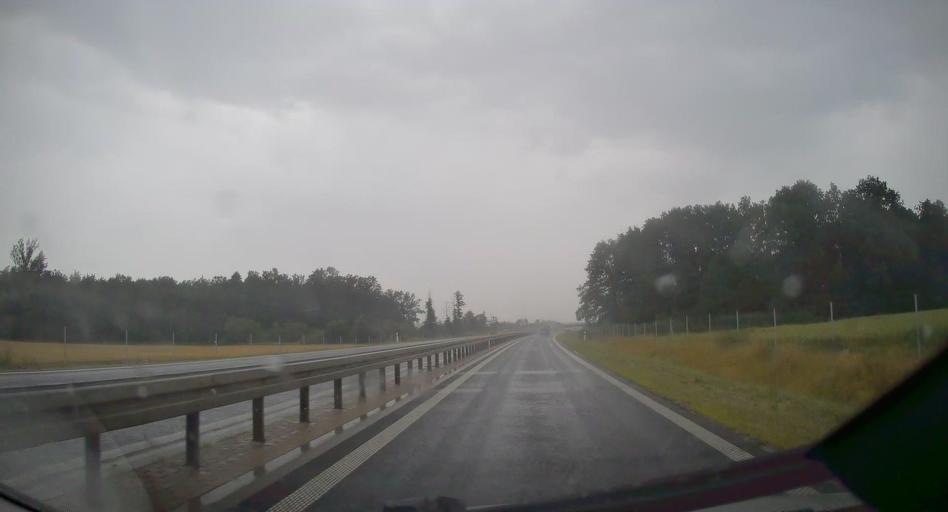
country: PL
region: Opole Voivodeship
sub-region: Powiat nyski
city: Nysa
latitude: 50.4575
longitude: 17.4037
